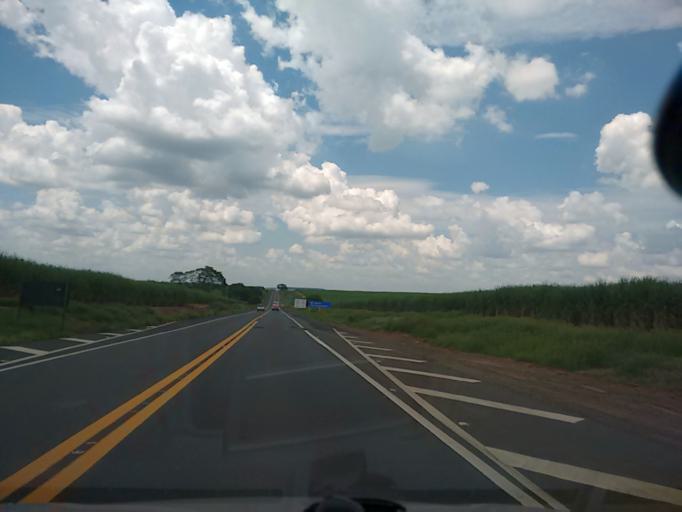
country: BR
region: Sao Paulo
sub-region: Osvaldo Cruz
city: Osvaldo Cruz
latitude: -21.9067
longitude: -50.8877
